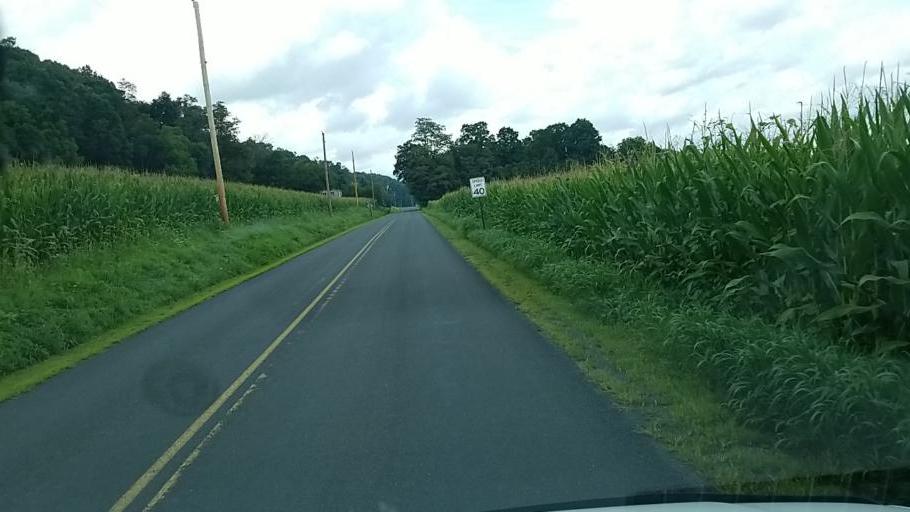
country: US
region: Pennsylvania
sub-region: Dauphin County
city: Elizabethville
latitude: 40.6503
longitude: -76.8591
